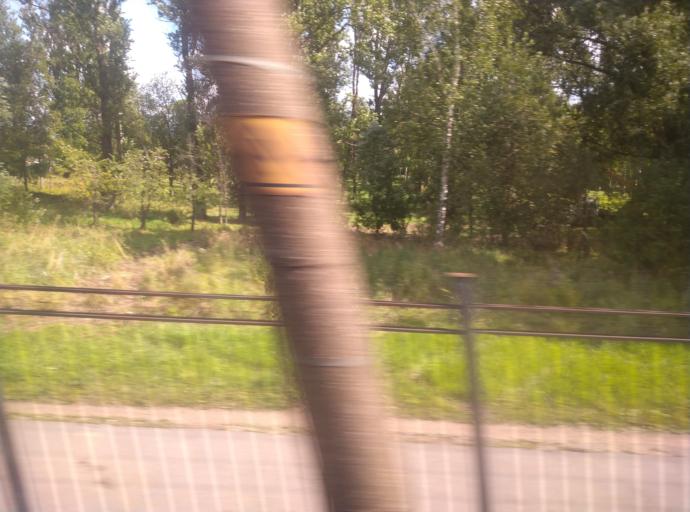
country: RU
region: St.-Petersburg
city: Kolpino
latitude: 59.7510
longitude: 30.6127
